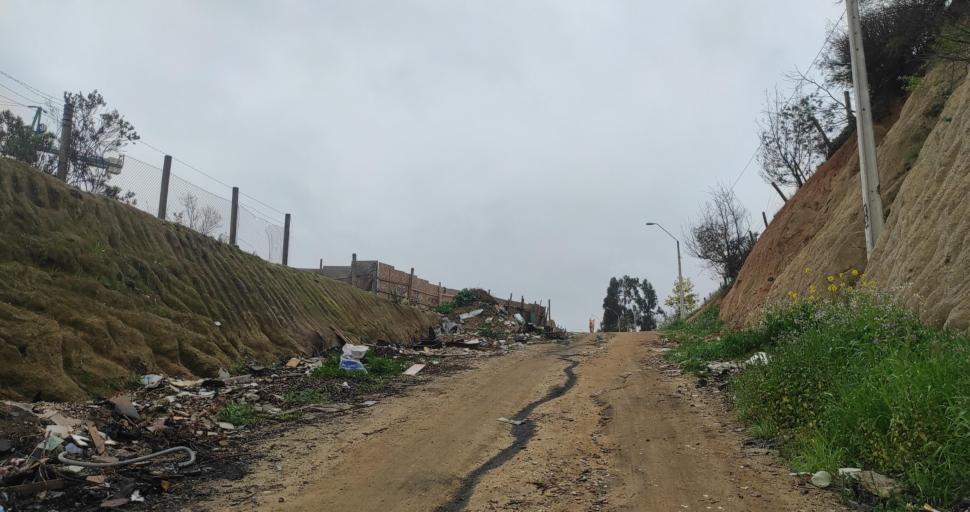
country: CL
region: Valparaiso
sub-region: Provincia de Marga Marga
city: Limache
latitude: -33.0193
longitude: -71.2612
